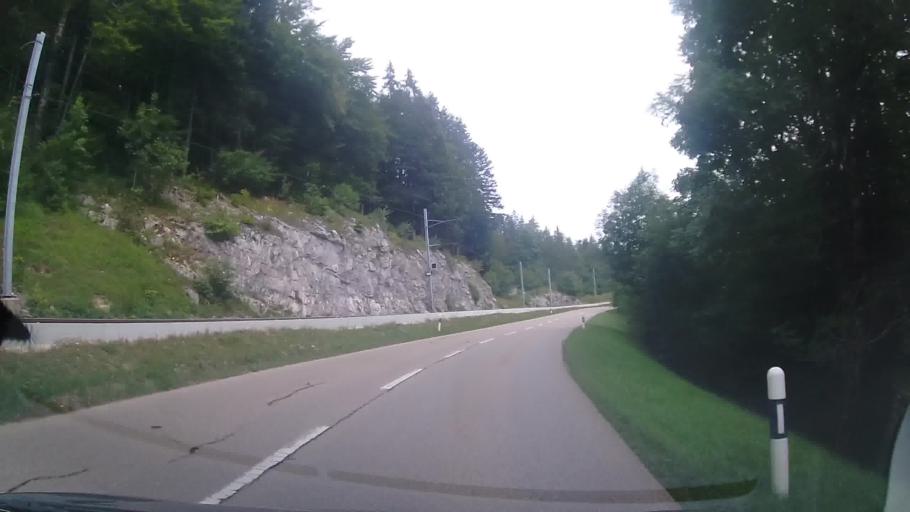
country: CH
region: Vaud
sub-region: Nyon District
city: Saint-Cergue
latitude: 46.4496
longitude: 6.1324
